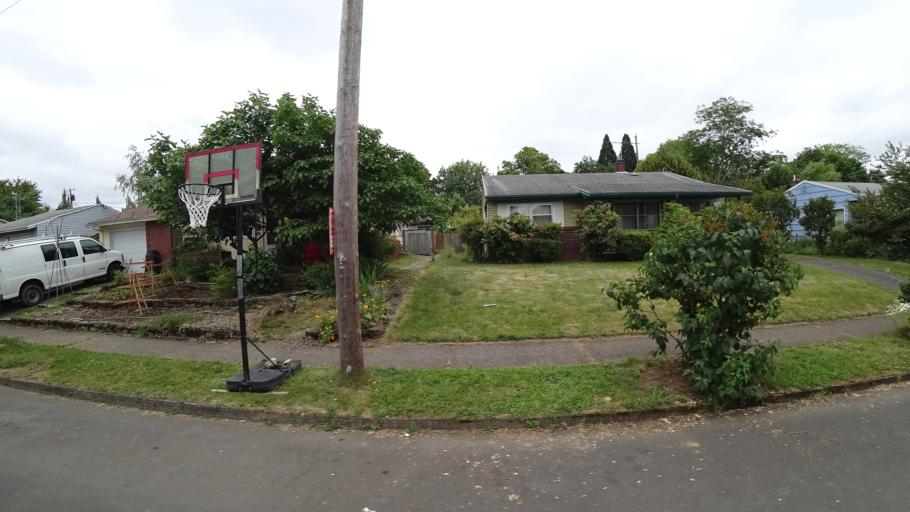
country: US
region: Oregon
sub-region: Multnomah County
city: Lents
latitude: 45.5072
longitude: -122.5822
